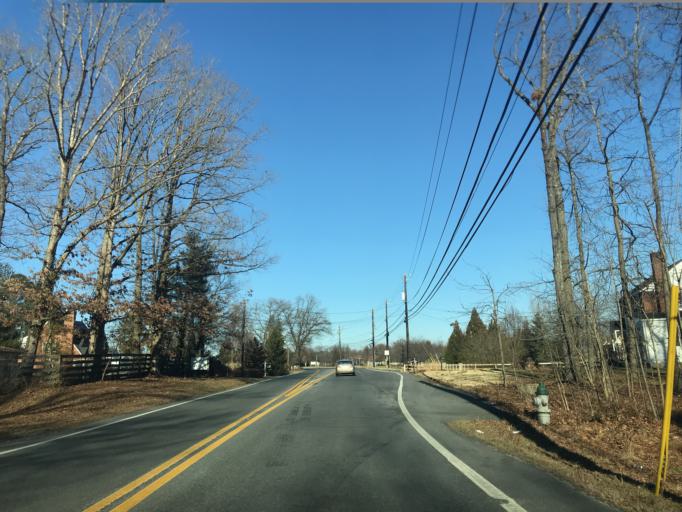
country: US
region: Maryland
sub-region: Prince George's County
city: Friendly
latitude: 38.7213
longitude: -76.9548
